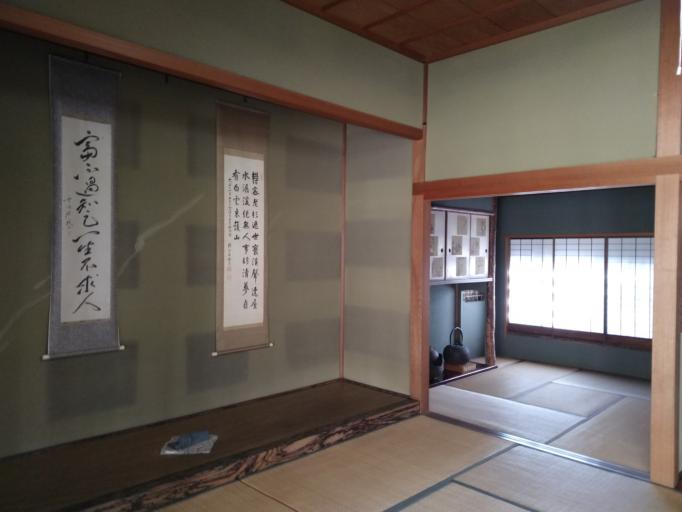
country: JP
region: Niigata
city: Tochio-honcho
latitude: 37.3219
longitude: 139.0154
